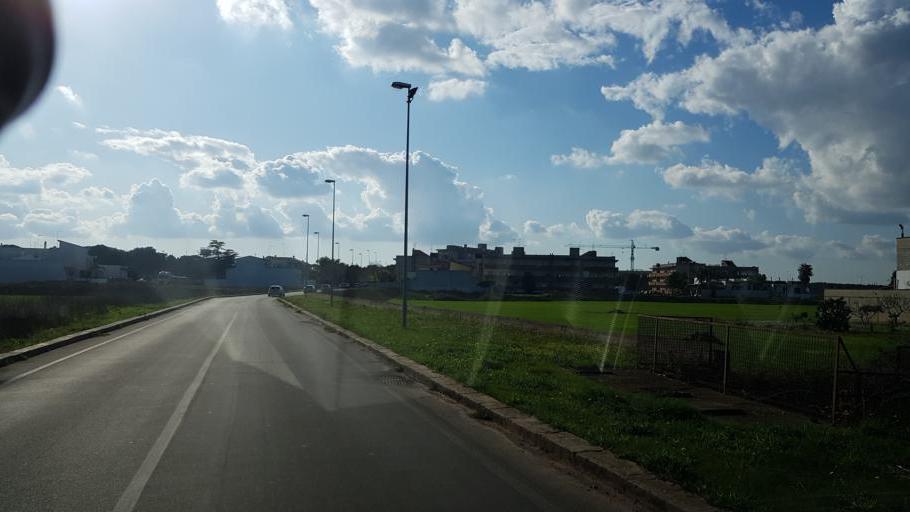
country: IT
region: Apulia
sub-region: Provincia di Lecce
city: Campi Salentina
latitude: 40.4058
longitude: 18.0181
